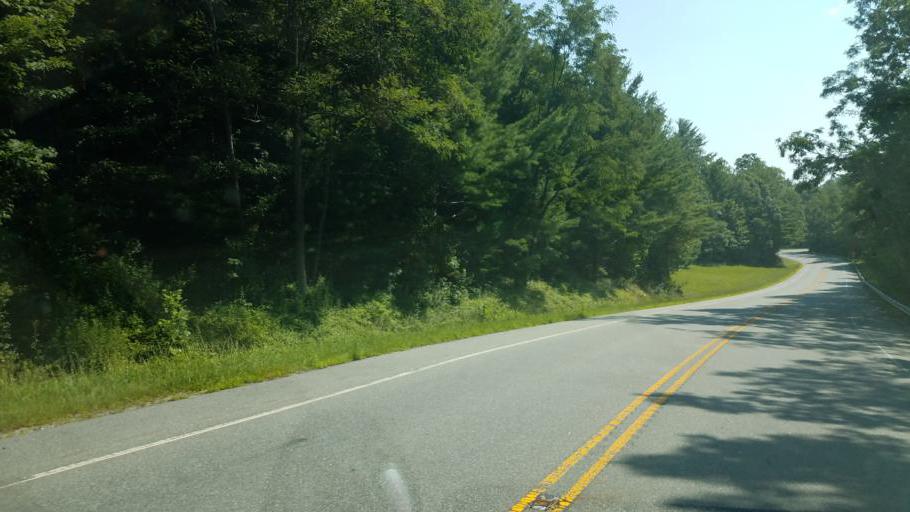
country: US
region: North Carolina
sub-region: Avery County
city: Newland
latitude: 35.9547
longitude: -81.8558
